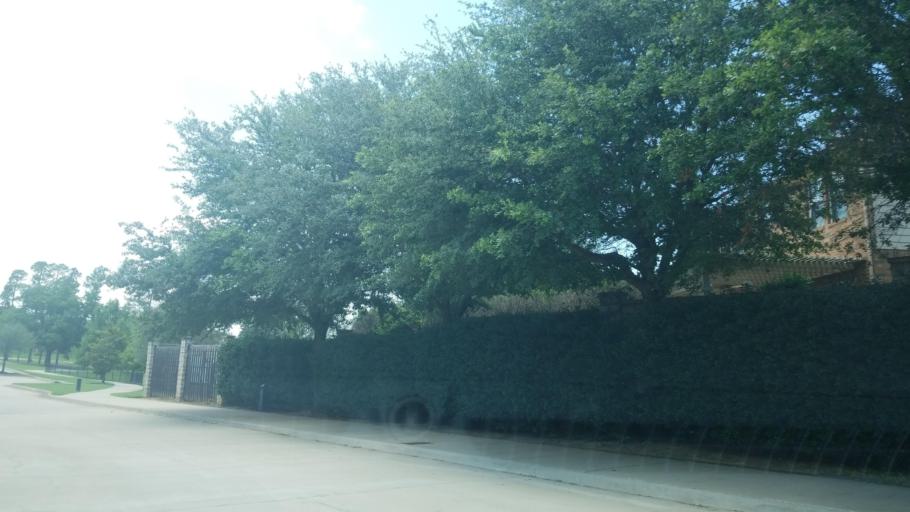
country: US
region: Texas
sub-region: Denton County
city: Copper Canyon
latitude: 33.0758
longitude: -97.0853
